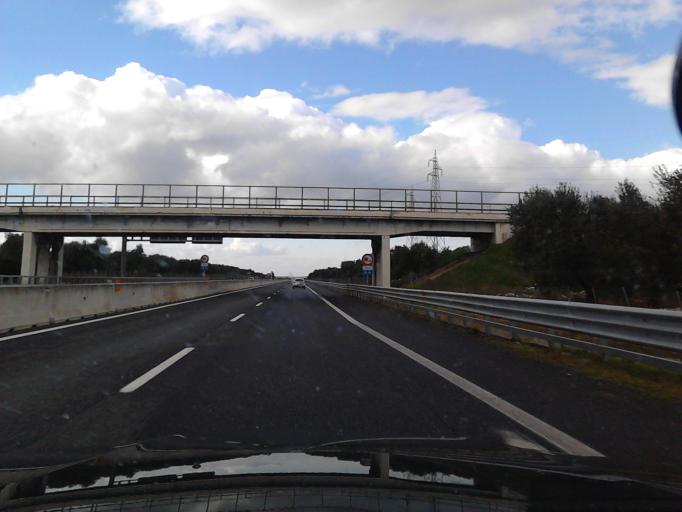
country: IT
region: Apulia
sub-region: Provincia di Barletta - Andria - Trani
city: Andria
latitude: 41.2553
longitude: 16.2864
